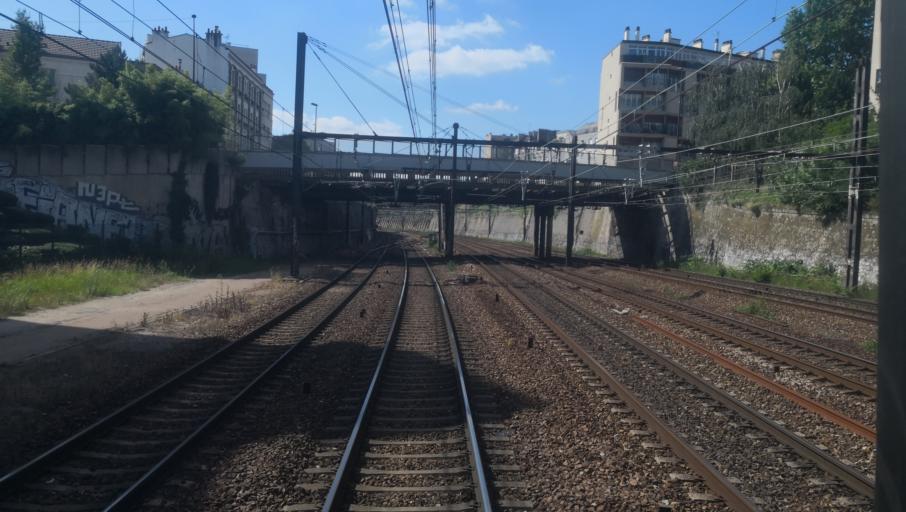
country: FR
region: Ile-de-France
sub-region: Departement du Val-de-Marne
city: Charenton-le-Pont
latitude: 48.8201
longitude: 2.4128
